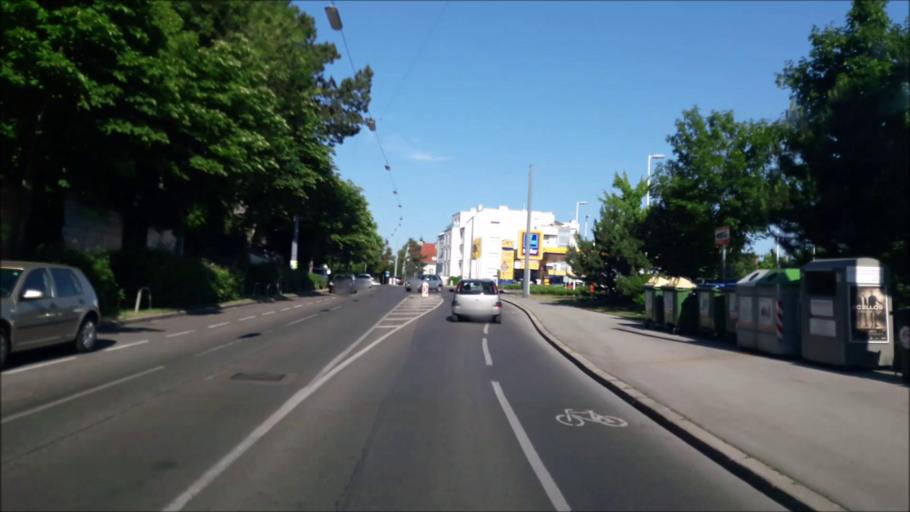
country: AT
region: Lower Austria
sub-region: Politischer Bezirk Wien-Umgebung
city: Purkersdorf
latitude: 48.2034
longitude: 16.2431
